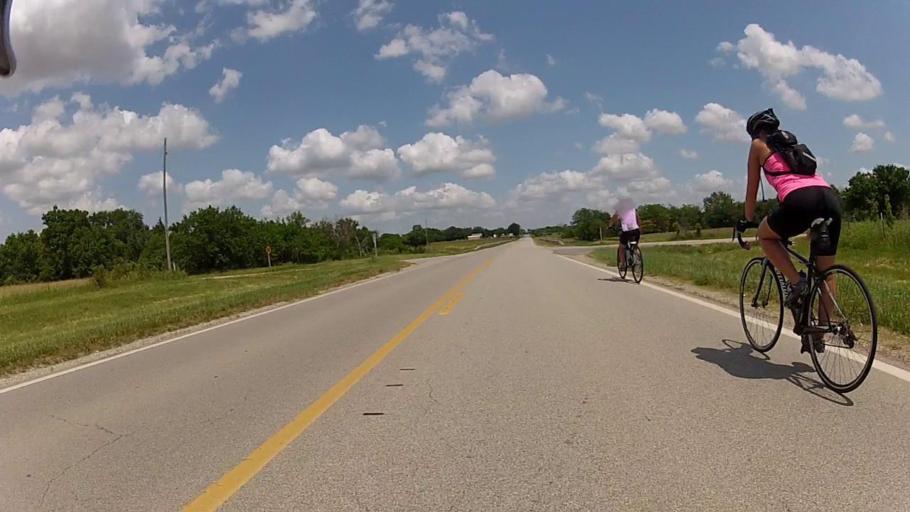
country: US
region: Kansas
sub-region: Labette County
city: Altamont
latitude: 37.1932
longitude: -95.3225
